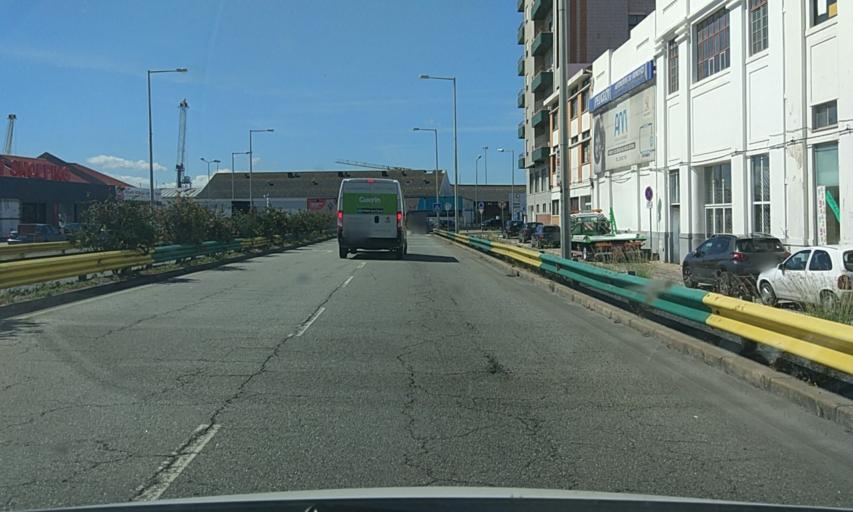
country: PT
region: Coimbra
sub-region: Figueira da Foz
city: Figueira da Foz
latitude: 40.1505
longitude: -8.8477
